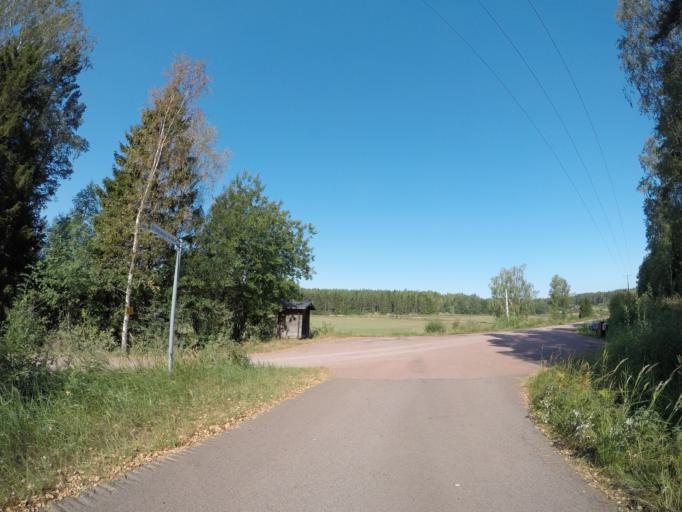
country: AX
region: Alands landsbygd
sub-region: Saltvik
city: Saltvik
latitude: 60.2241
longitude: 20.0107
